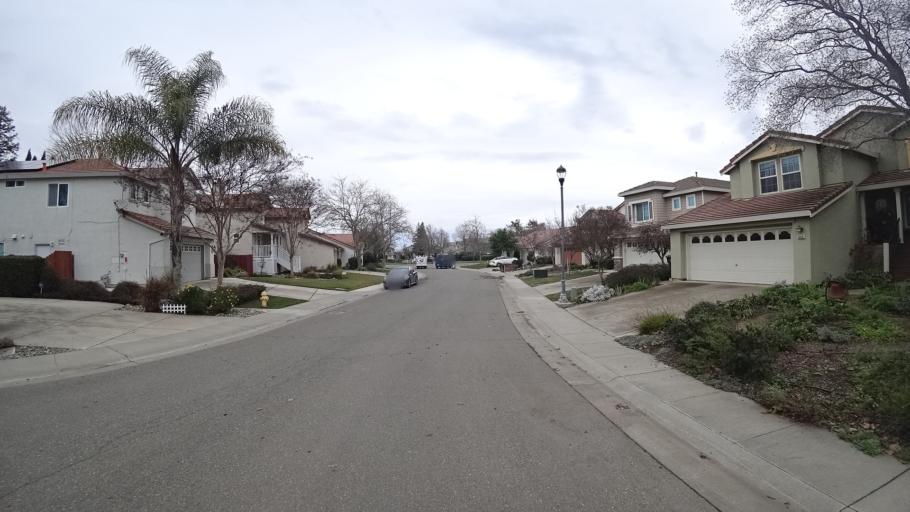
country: US
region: California
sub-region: Yolo County
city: Davis
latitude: 38.5583
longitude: -121.7021
